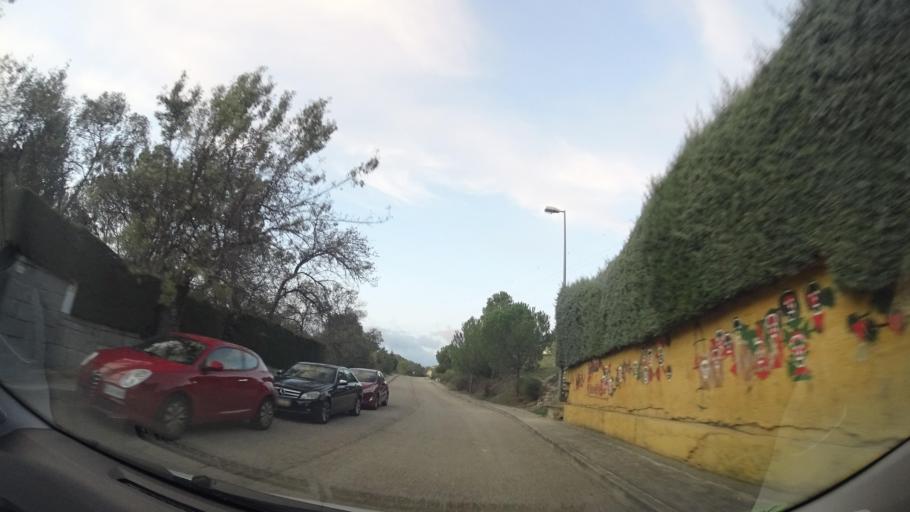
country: ES
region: Madrid
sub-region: Provincia de Madrid
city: Colmenarejo
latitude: 40.5593
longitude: -4.0234
